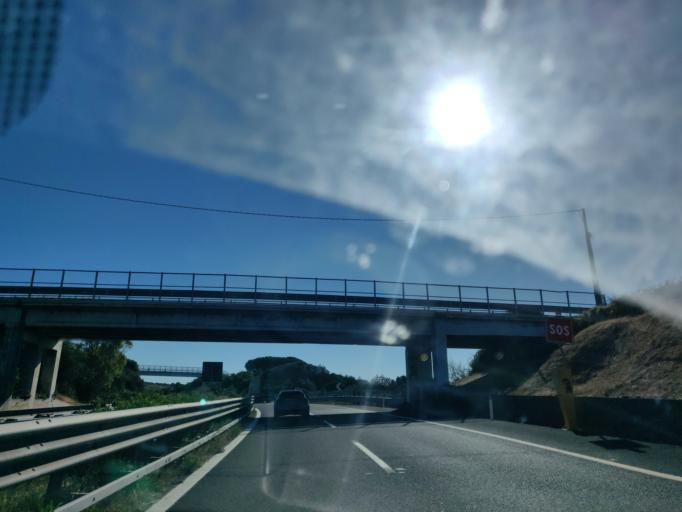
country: IT
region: Latium
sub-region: Citta metropolitana di Roma Capitale
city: Santa Marinella
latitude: 42.0396
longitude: 11.8525
